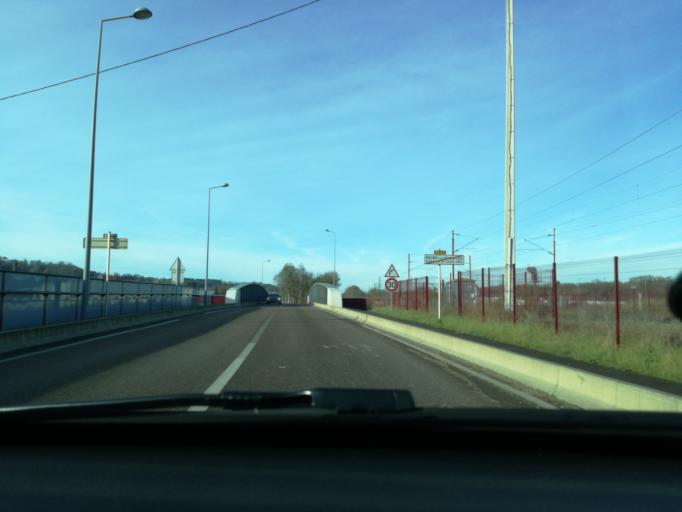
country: FR
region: Lorraine
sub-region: Departement de la Meuse
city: Fains-Veel
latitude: 48.7871
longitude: 5.1403
